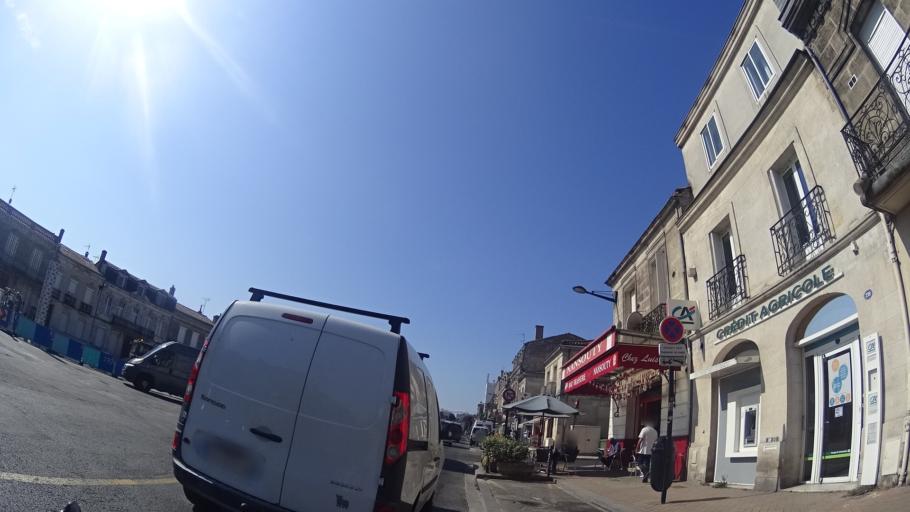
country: FR
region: Aquitaine
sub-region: Departement de la Gironde
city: Bordeaux
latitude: 44.8203
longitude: -0.5724
